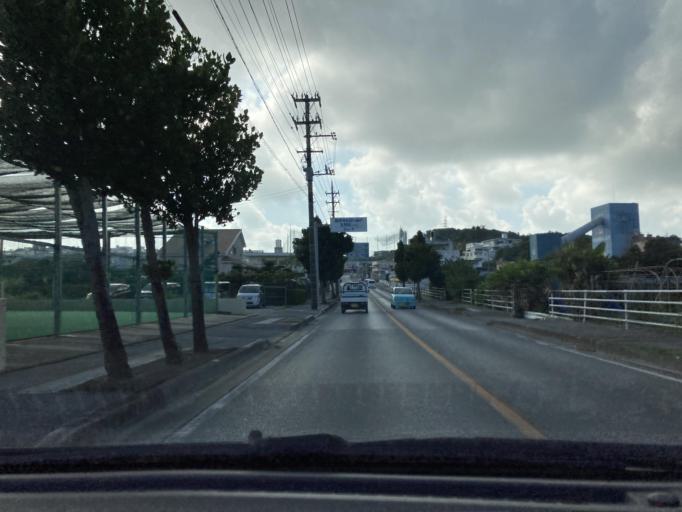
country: JP
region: Okinawa
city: Tomigusuku
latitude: 26.1706
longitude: 127.7381
